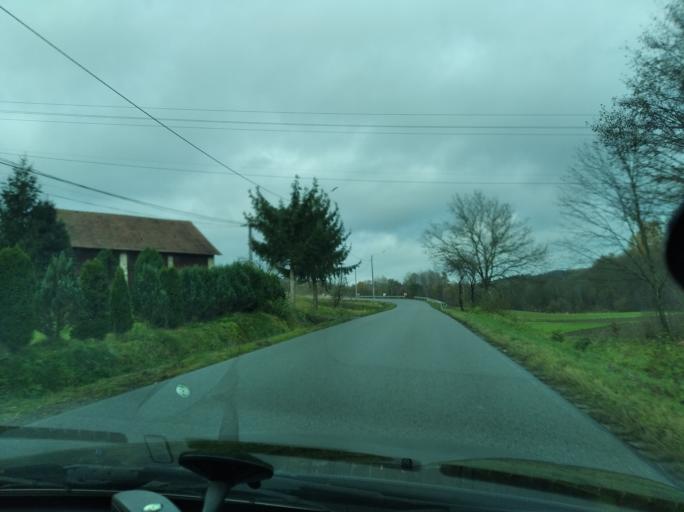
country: PL
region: Subcarpathian Voivodeship
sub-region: Powiat strzyzowski
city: Wisniowa
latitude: 49.9330
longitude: 21.7077
